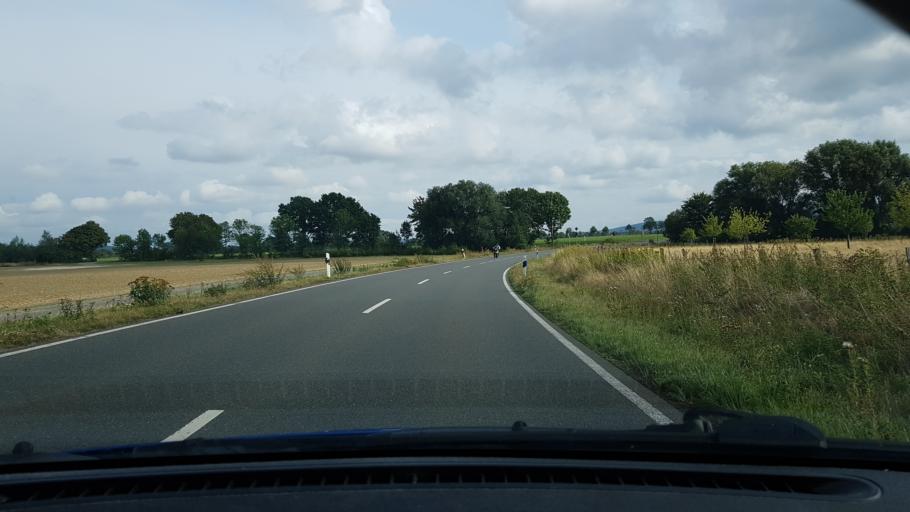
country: DE
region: Lower Saxony
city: Egestorf
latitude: 52.3051
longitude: 9.5030
